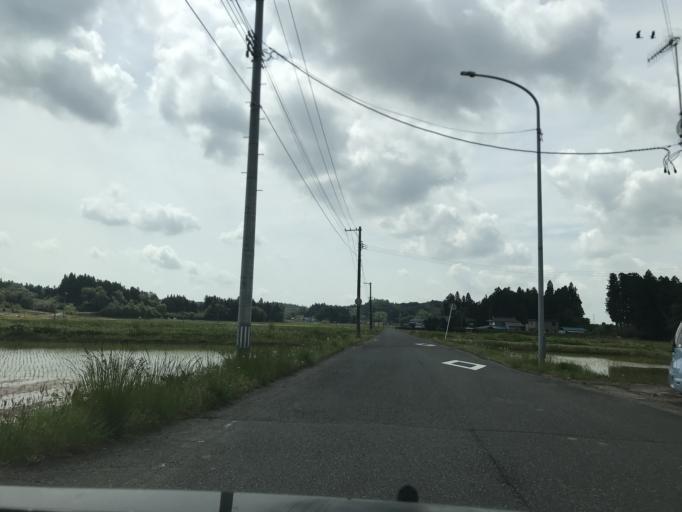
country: JP
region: Iwate
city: Ichinoseki
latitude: 38.8487
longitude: 141.0176
